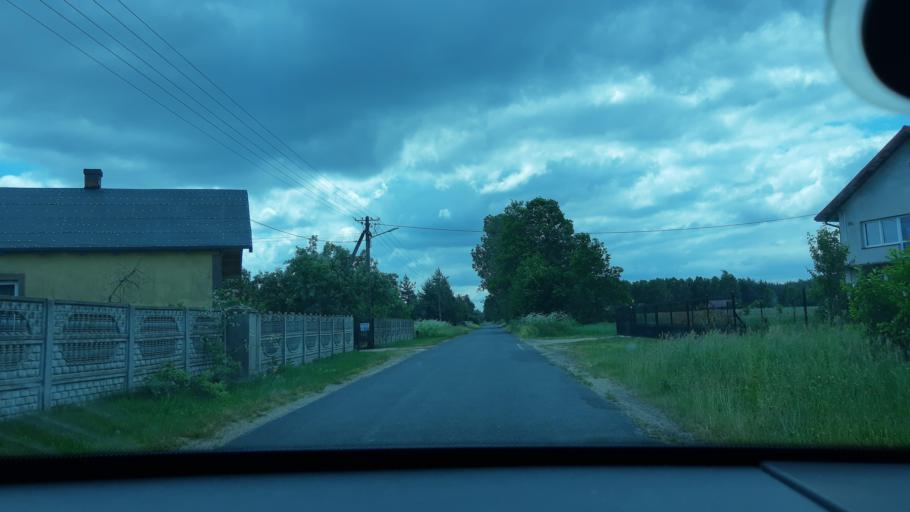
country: PL
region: Lodz Voivodeship
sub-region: Powiat zdunskowolski
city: Zapolice
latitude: 51.5228
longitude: 18.8434
